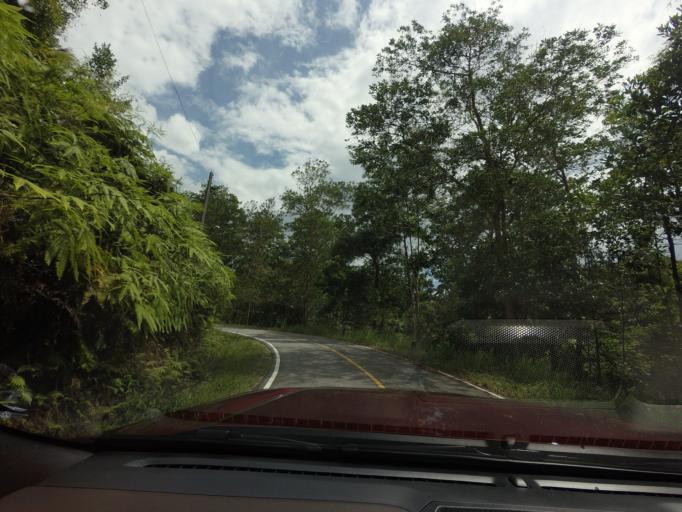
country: TH
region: Narathiwat
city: Sukhirin
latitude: 5.9342
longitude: 101.6502
